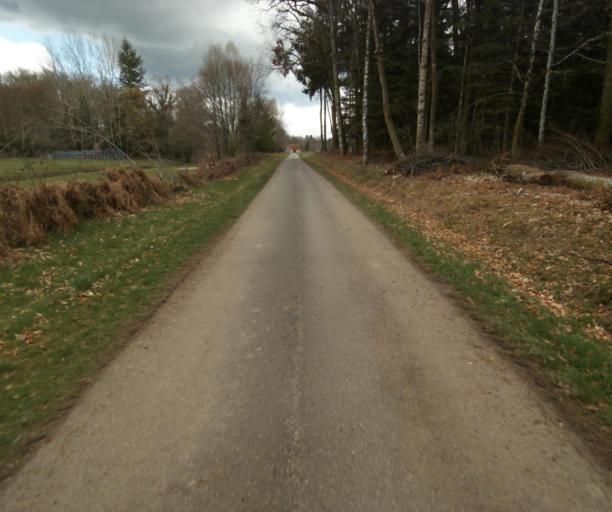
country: FR
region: Limousin
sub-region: Departement de la Correze
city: Correze
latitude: 45.2608
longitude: 1.9037
